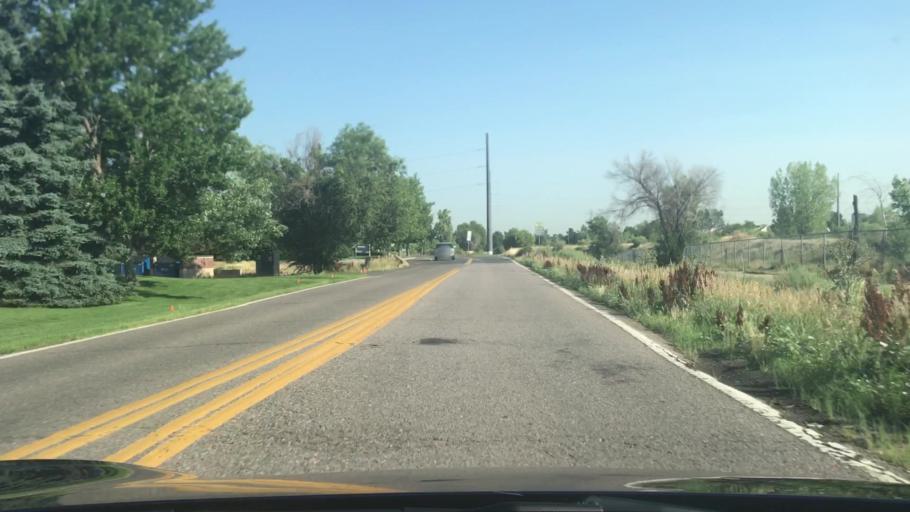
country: US
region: Colorado
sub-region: Arapahoe County
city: Glendale
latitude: 39.6780
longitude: -104.8959
